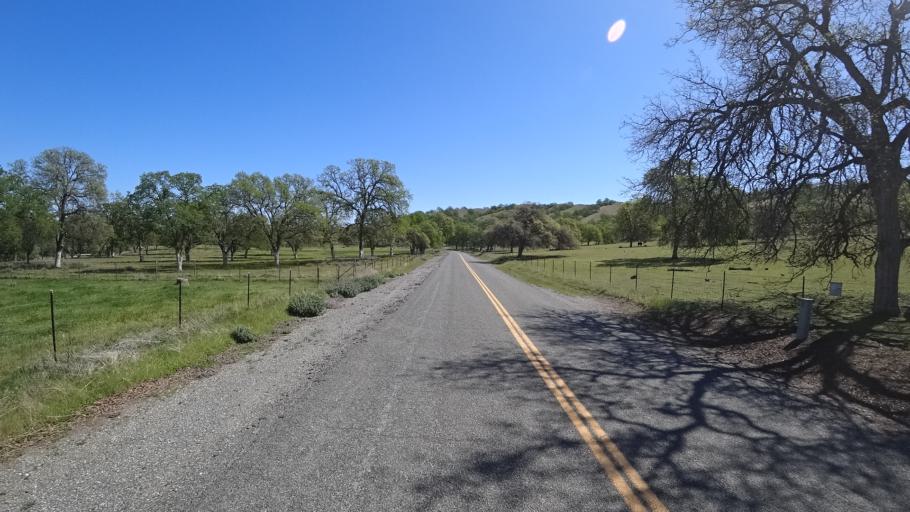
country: US
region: California
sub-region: Glenn County
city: Orland
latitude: 39.7315
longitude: -122.4084
